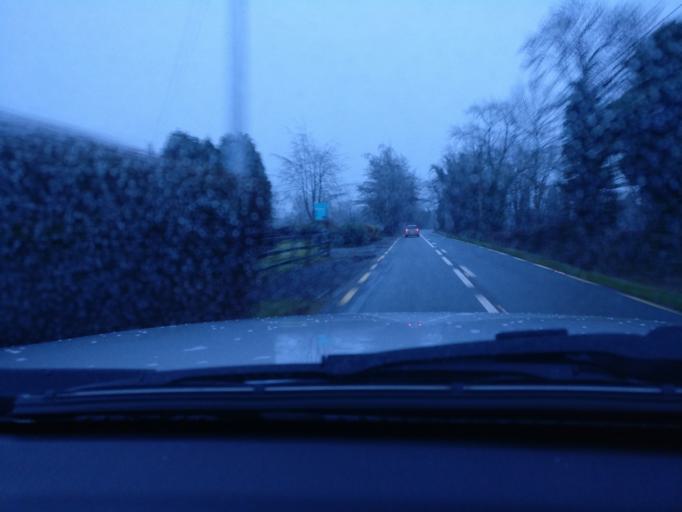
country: IE
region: Leinster
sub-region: An Mhi
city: Athboy
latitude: 53.6407
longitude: -6.8361
